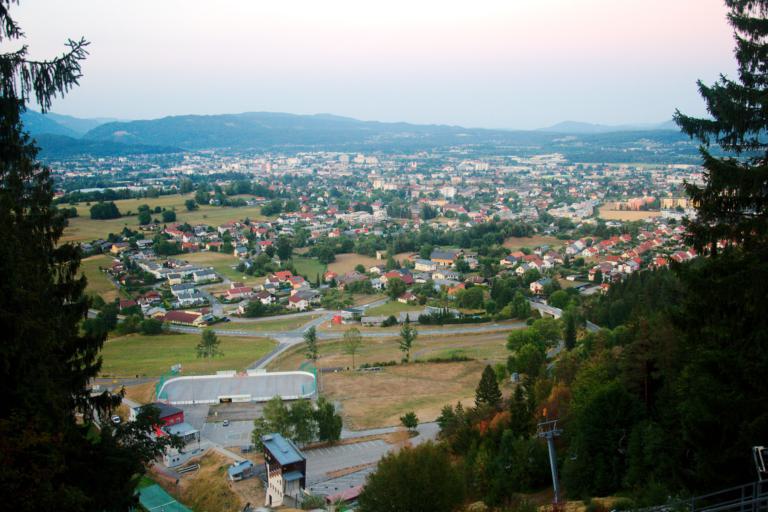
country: AT
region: Carinthia
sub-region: Villach Stadt
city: Villach
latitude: 46.6021
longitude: 13.8085
